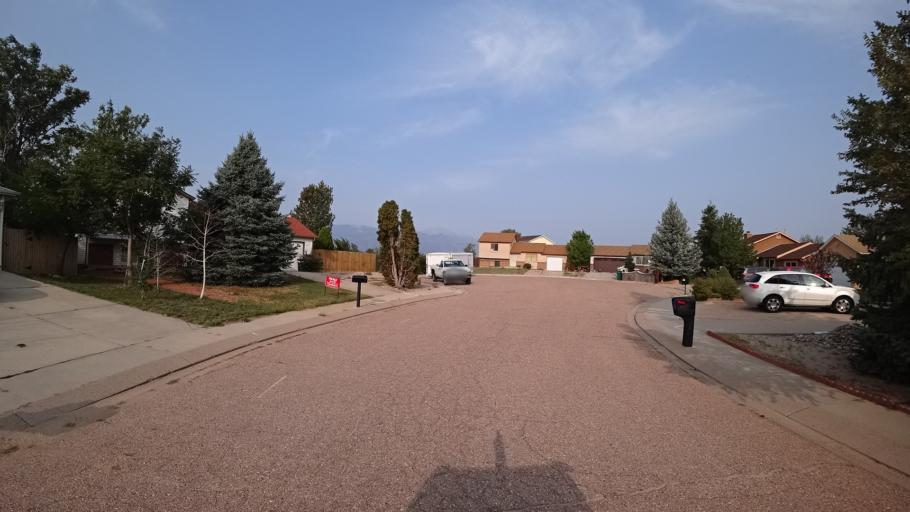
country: US
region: Colorado
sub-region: El Paso County
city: Stratmoor
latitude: 38.8048
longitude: -104.7383
